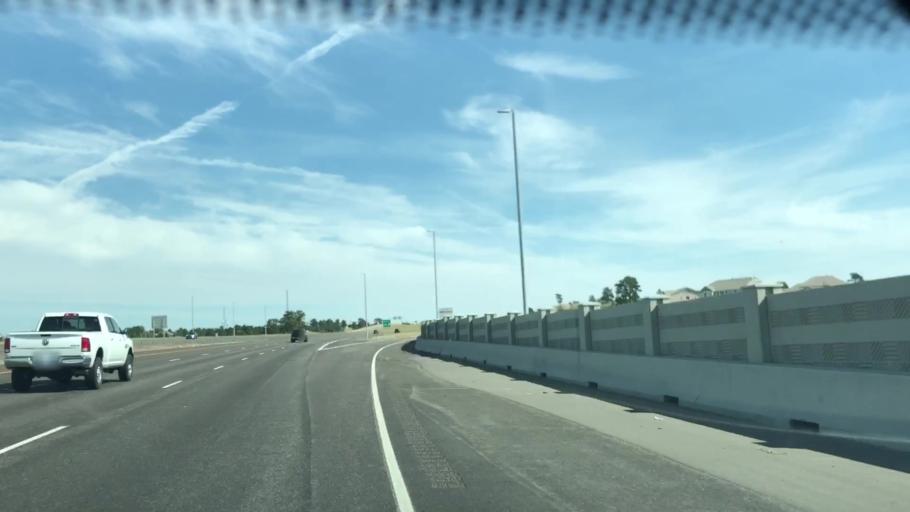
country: US
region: Colorado
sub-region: Douglas County
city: Parker
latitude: 39.5919
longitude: -104.7196
